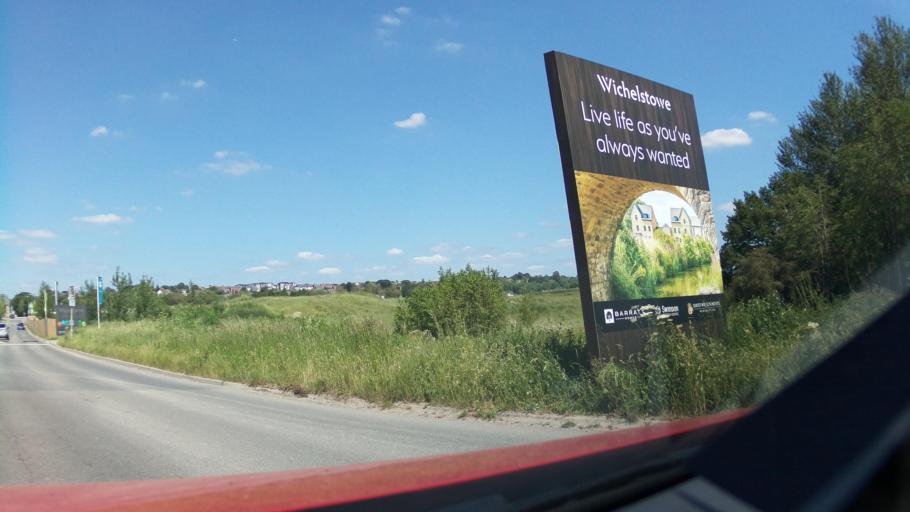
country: GB
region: England
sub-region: Borough of Swindon
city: Wroughton
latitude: 51.5424
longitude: -1.8084
